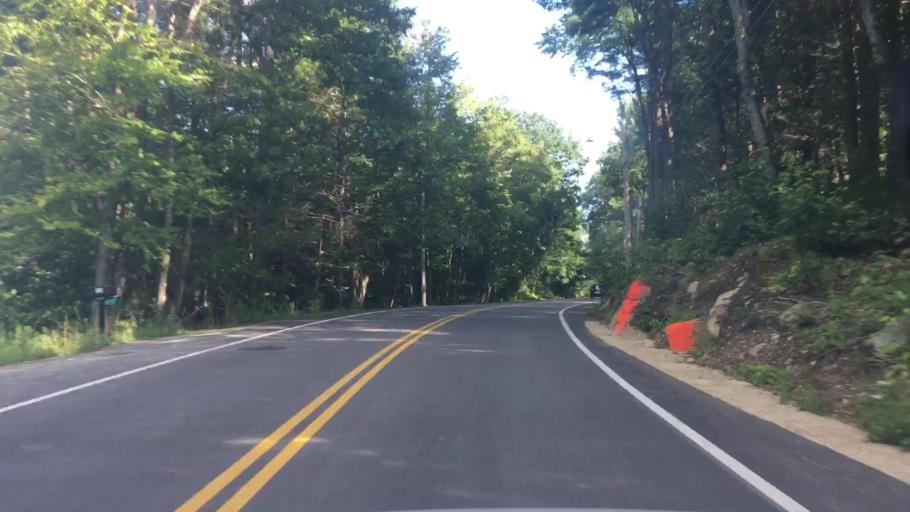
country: US
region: New Hampshire
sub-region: Strafford County
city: Dover
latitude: 43.1644
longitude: -70.8817
